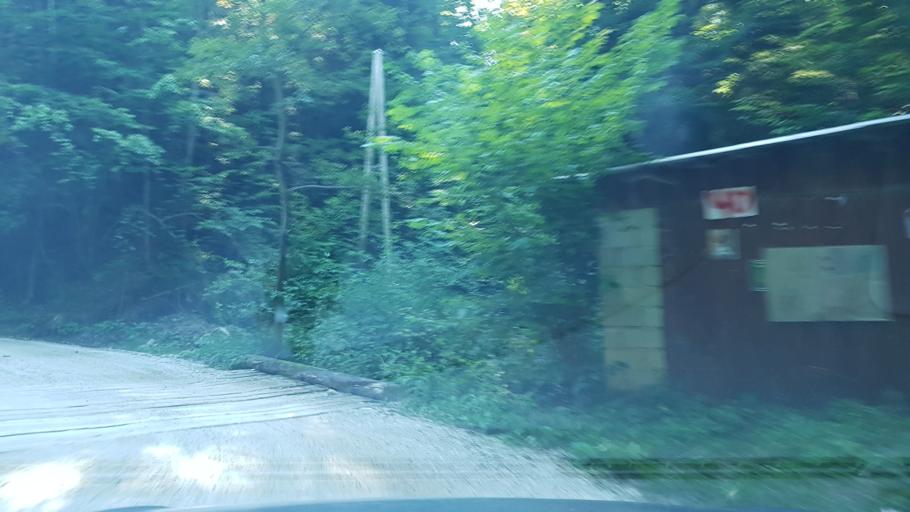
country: SI
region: Ravne na Koroskem
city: Kotlje
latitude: 46.5026
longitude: 14.9488
